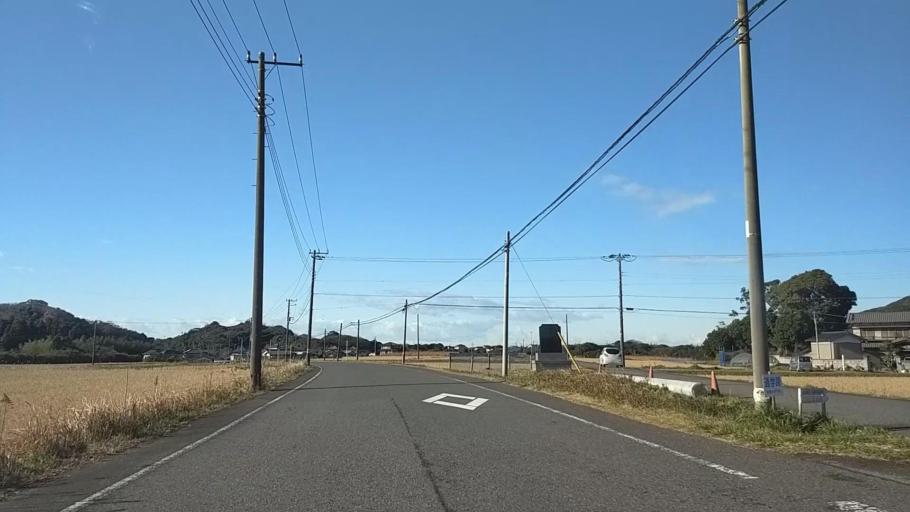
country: JP
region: Chiba
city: Kimitsu
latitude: 35.2567
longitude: 139.8746
